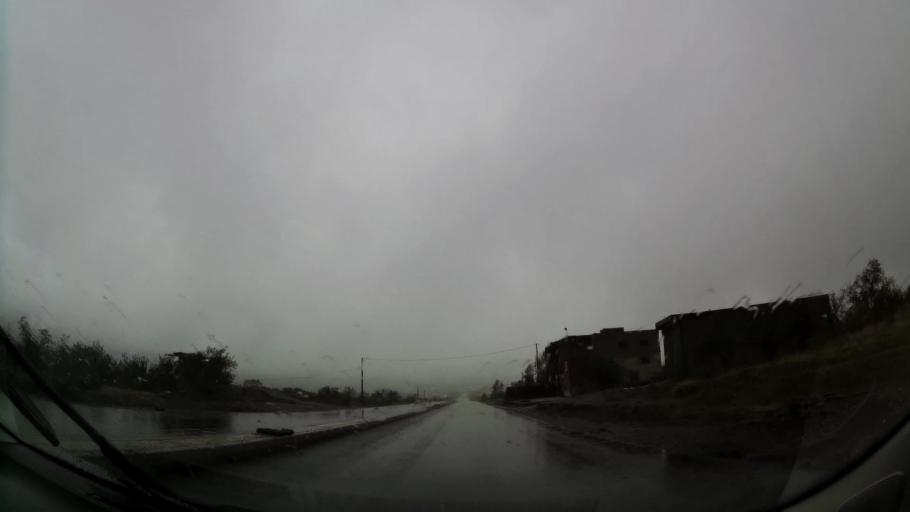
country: MA
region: Oriental
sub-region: Nador
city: Midar
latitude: 34.8460
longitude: -3.7214
